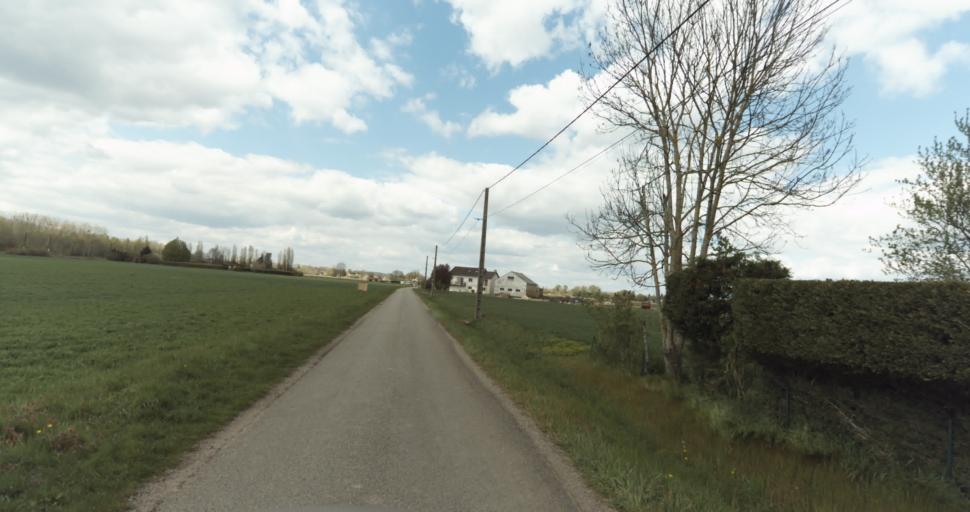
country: FR
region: Bourgogne
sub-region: Departement de la Cote-d'Or
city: Auxonne
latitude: 47.1760
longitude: 5.3944
